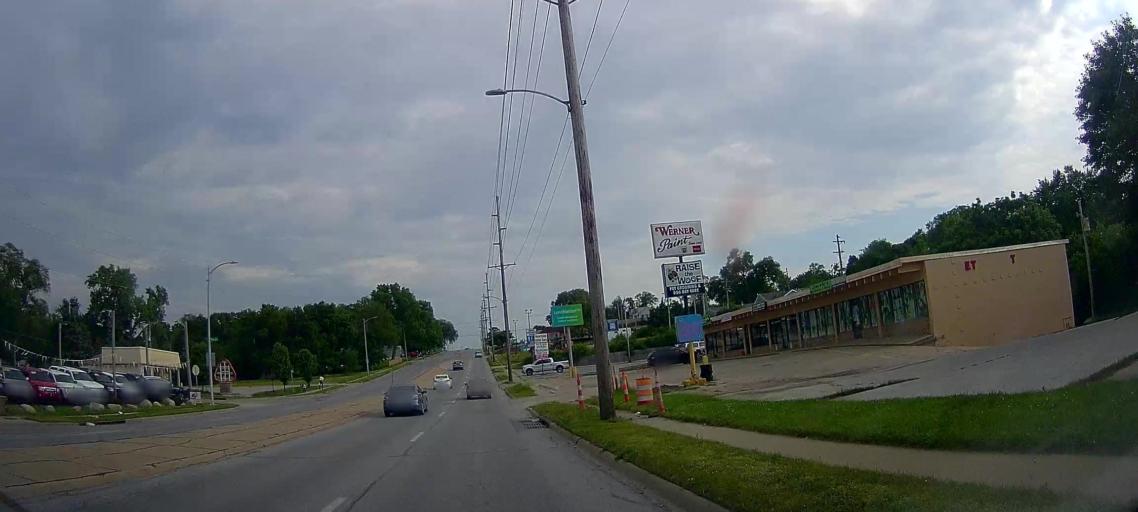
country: US
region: Nebraska
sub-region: Douglas County
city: Ralston
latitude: 41.2829
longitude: -96.0240
